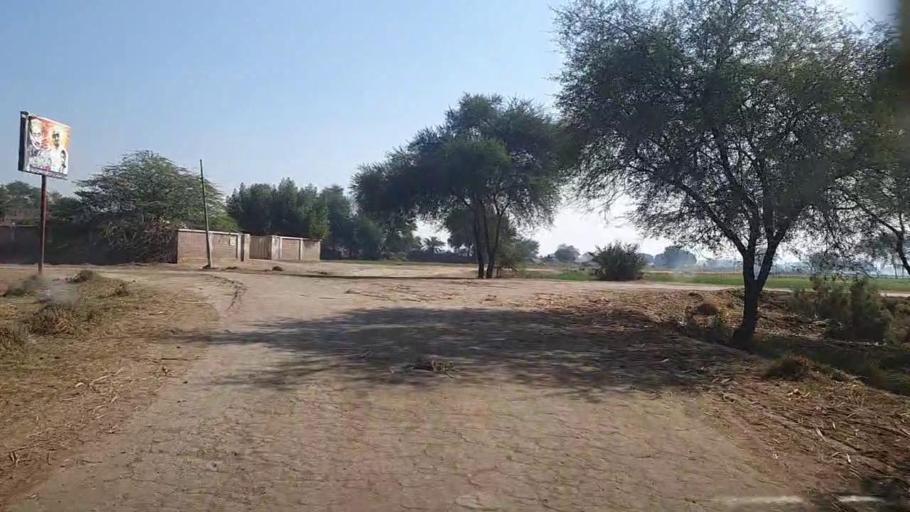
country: PK
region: Sindh
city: Khairpur
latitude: 27.9532
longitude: 69.6877
